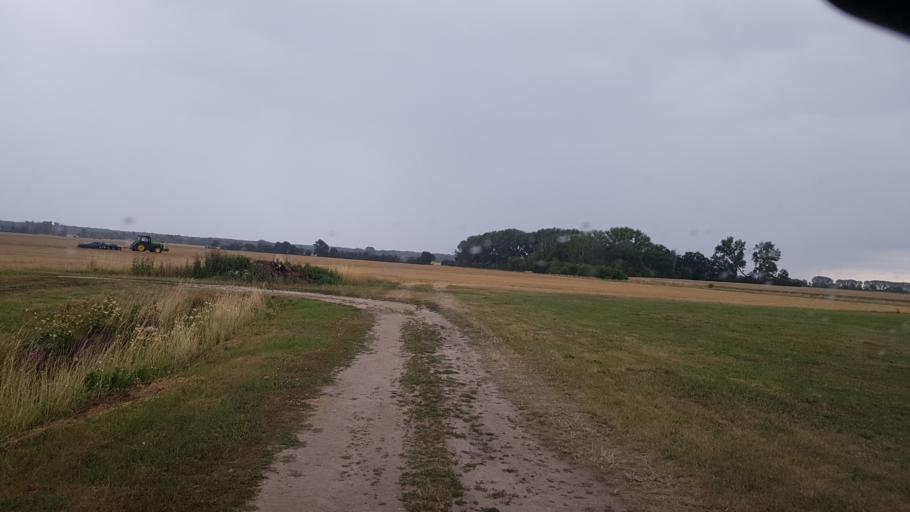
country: DE
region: Brandenburg
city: Sonnewalde
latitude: 51.7035
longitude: 13.6999
